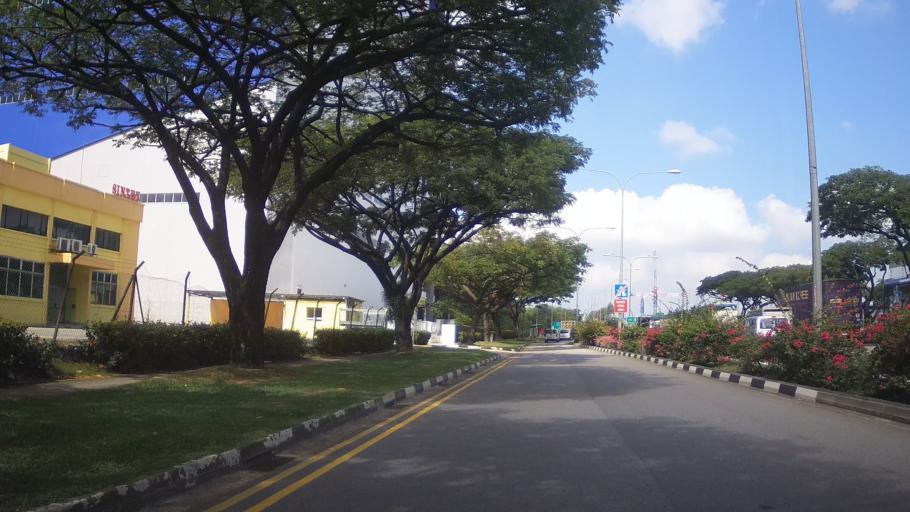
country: SG
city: Singapore
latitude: 1.3221
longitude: 103.7003
